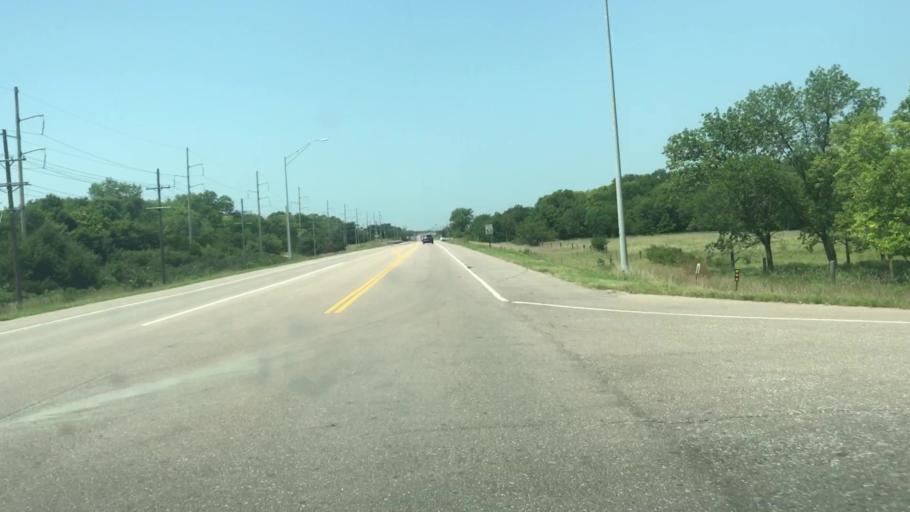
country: US
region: Nebraska
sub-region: Hall County
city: Grand Island
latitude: 40.8876
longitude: -98.3591
